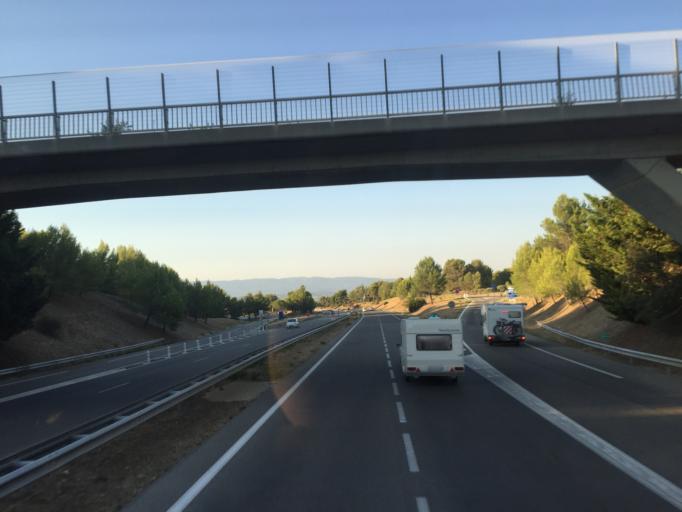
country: FR
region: Provence-Alpes-Cote d'Azur
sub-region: Departement des Bouches-du-Rhone
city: Venelles
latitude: 43.6293
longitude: 5.4934
